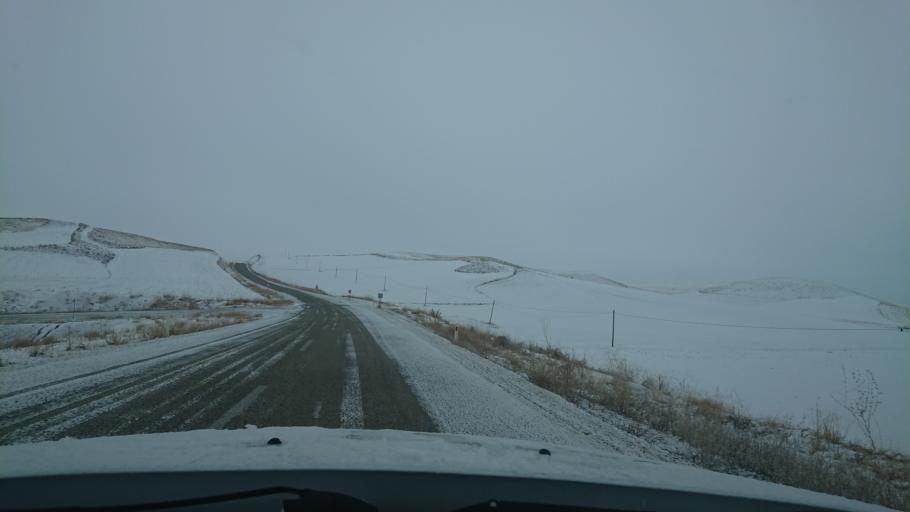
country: TR
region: Aksaray
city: Agacoren
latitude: 38.7870
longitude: 33.8711
